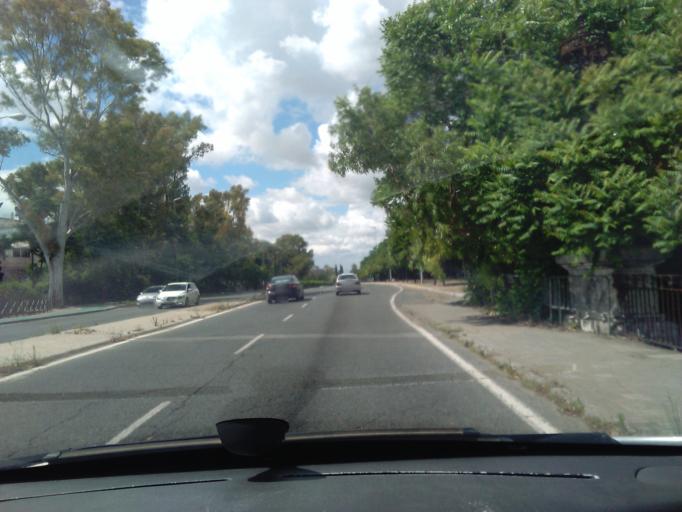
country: ES
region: Andalusia
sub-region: Provincia de Sevilla
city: Sevilla
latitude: 37.3533
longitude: -5.9782
